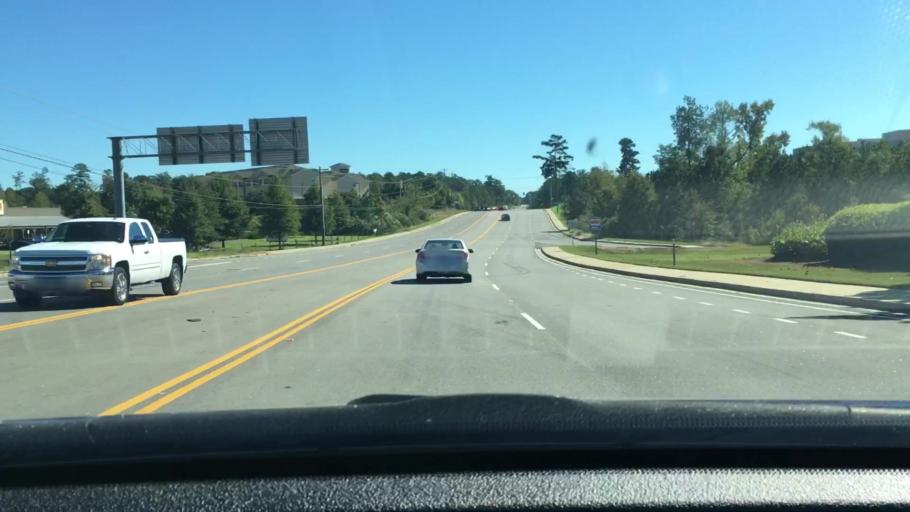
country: US
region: South Carolina
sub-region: Lexington County
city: Irmo
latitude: 34.0907
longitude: -81.1640
